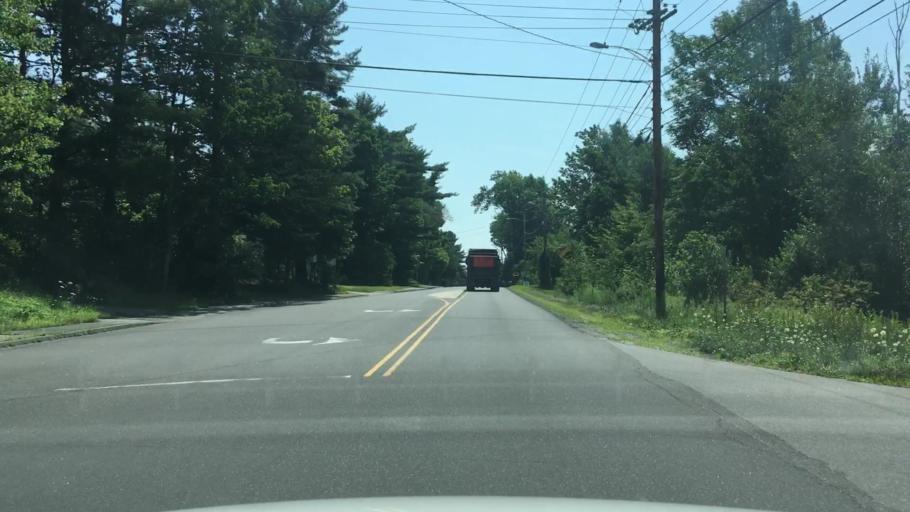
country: US
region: Maine
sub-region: Kennebec County
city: Hallowell
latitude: 44.2934
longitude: -69.8006
